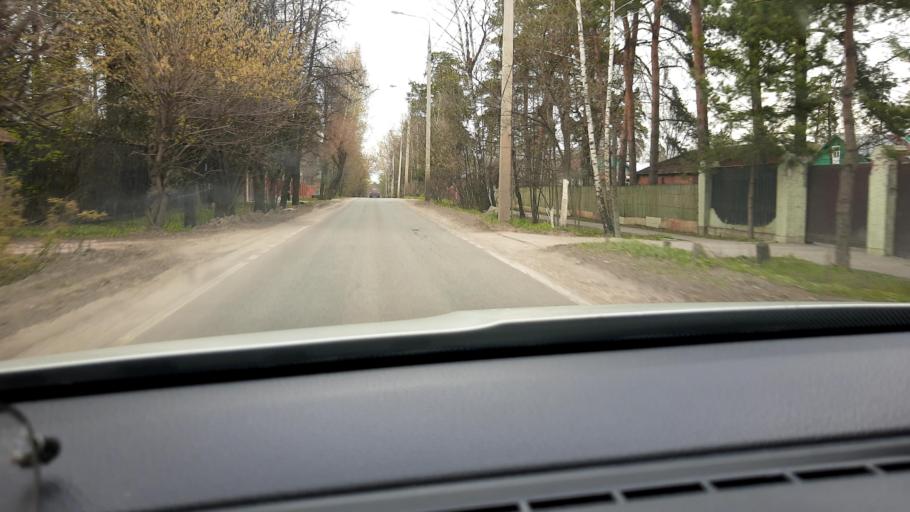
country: RU
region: Moskovskaya
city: Vidnoye
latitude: 55.5455
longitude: 37.6795
